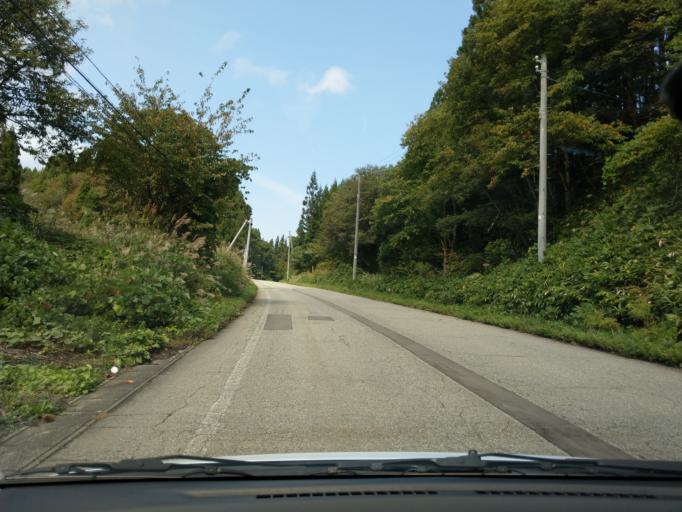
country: JP
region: Akita
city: Omagari
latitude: 39.5104
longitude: 140.3090
